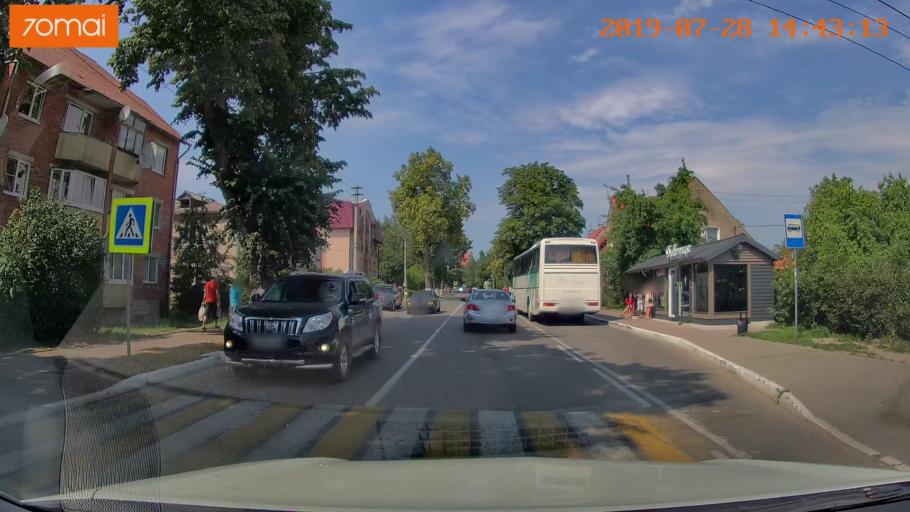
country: RU
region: Kaliningrad
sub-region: Gorod Kaliningrad
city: Yantarnyy
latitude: 54.8639
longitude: 19.9393
